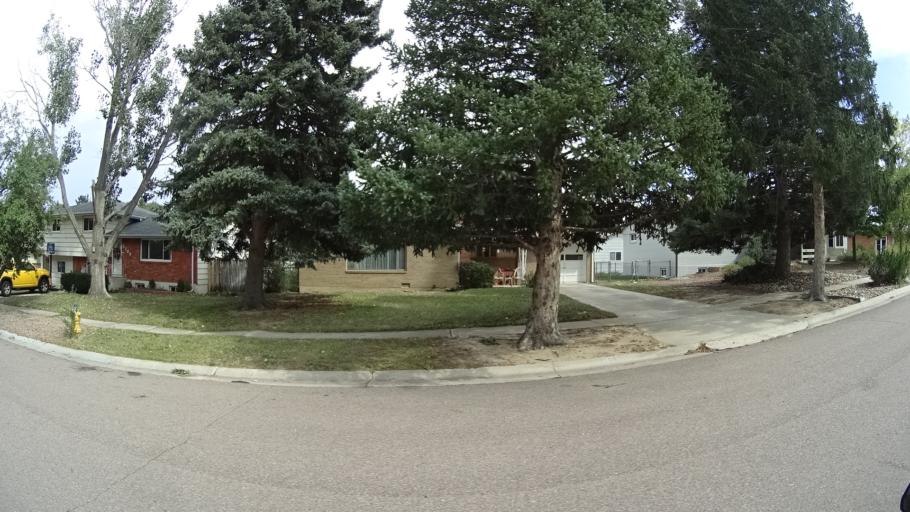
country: US
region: Colorado
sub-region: El Paso County
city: Colorado Springs
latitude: 38.8613
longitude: -104.7862
